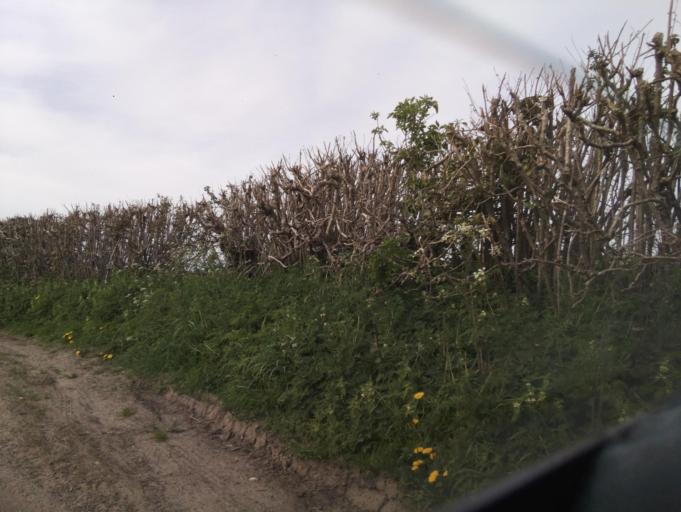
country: GB
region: England
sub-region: Dorset
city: Sherborne
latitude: 50.9706
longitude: -2.5070
